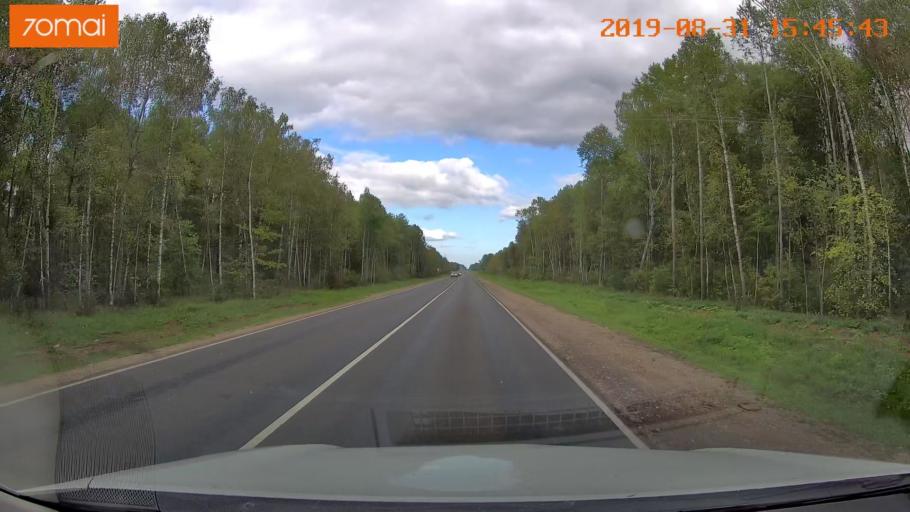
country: RU
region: Kaluga
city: Mosal'sk
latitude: 54.6681
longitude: 34.9661
